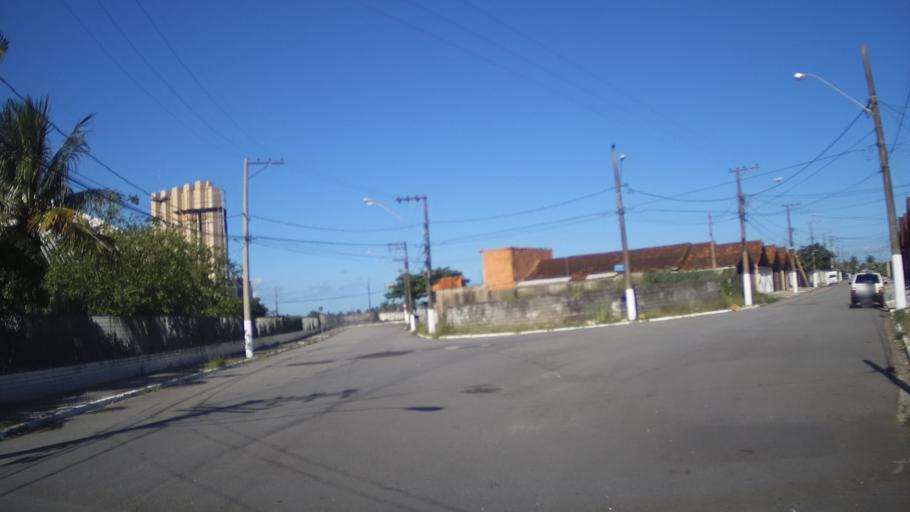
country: BR
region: Sao Paulo
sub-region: Praia Grande
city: Praia Grande
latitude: -24.0349
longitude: -46.4943
